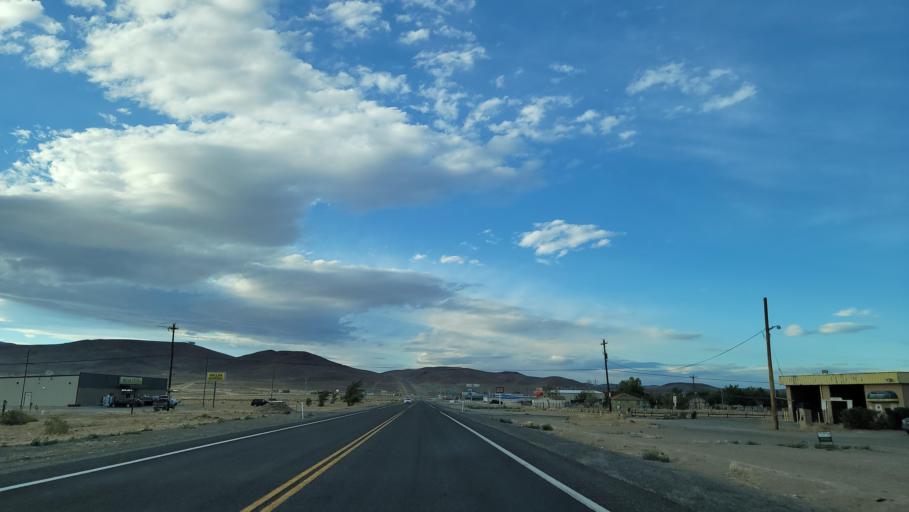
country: US
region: Nevada
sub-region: Lyon County
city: Silver Springs
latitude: 39.4035
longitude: -119.2276
